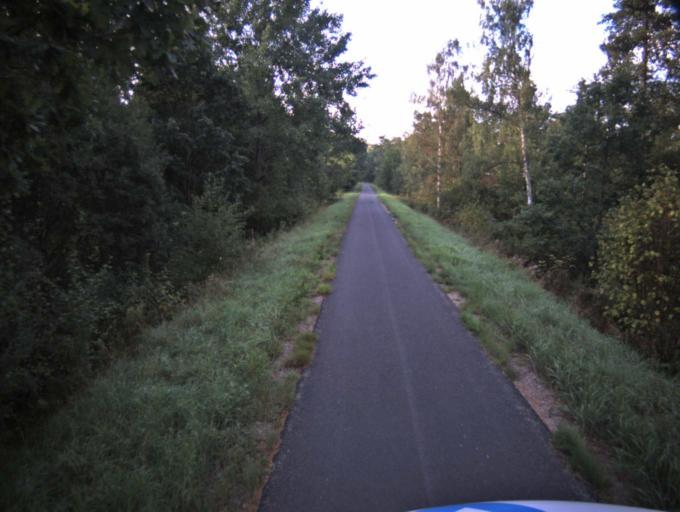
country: SE
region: Vaestra Goetaland
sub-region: Ulricehamns Kommun
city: Ulricehamn
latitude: 57.7486
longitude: 13.3934
